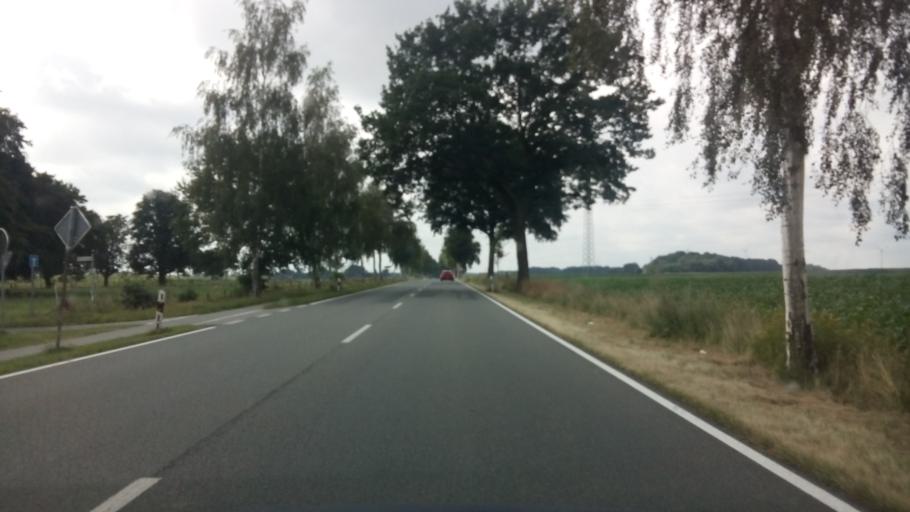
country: DE
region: Lower Saxony
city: Drentwede
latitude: 52.7439
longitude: 8.5634
